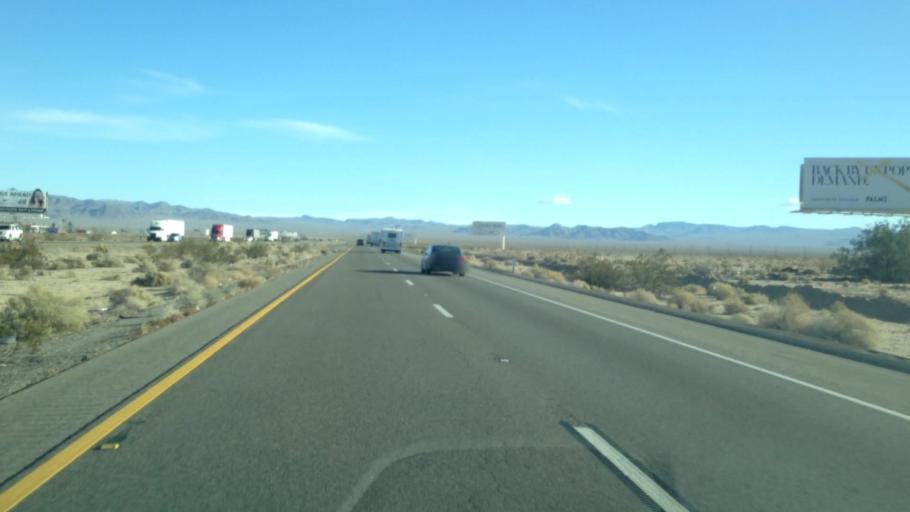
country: US
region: California
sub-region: San Bernardino County
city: Fort Irwin
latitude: 35.2692
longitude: -116.0633
